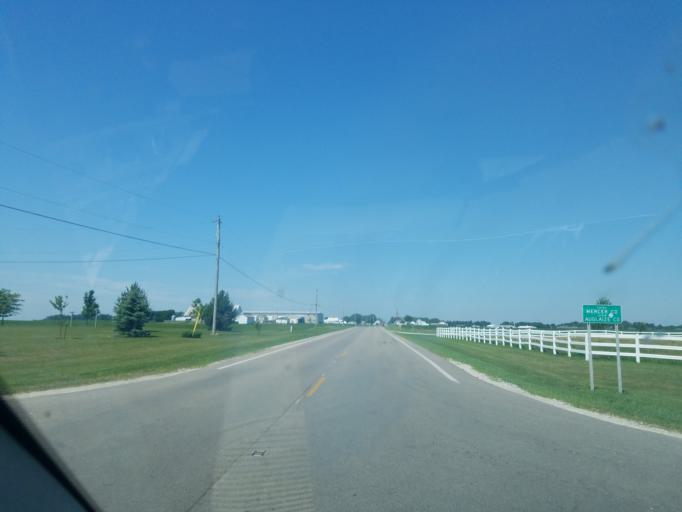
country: US
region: Ohio
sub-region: Auglaize County
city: Minster
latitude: 40.4075
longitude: -84.4554
